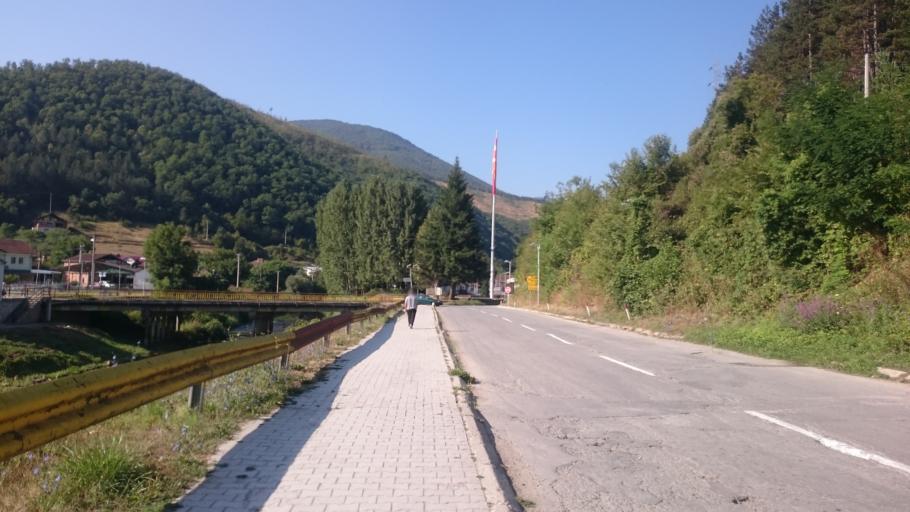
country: MK
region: Makedonski Brod
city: Makedonski Brod
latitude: 41.5080
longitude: 21.2162
